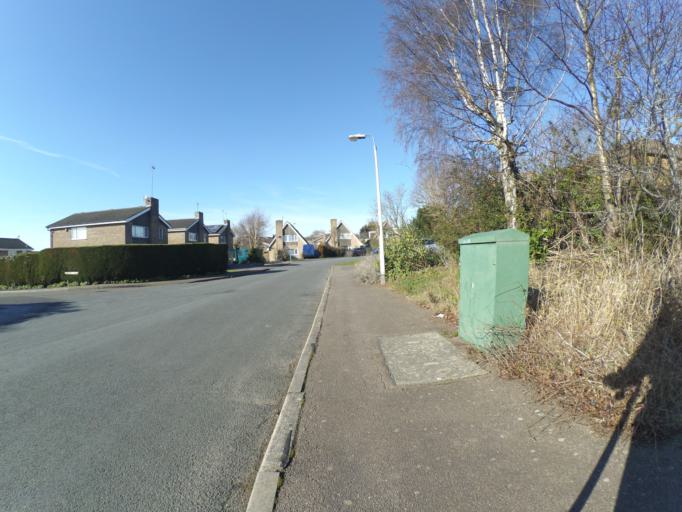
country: GB
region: England
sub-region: Warwickshire
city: Rugby
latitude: 52.3881
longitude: -1.2467
